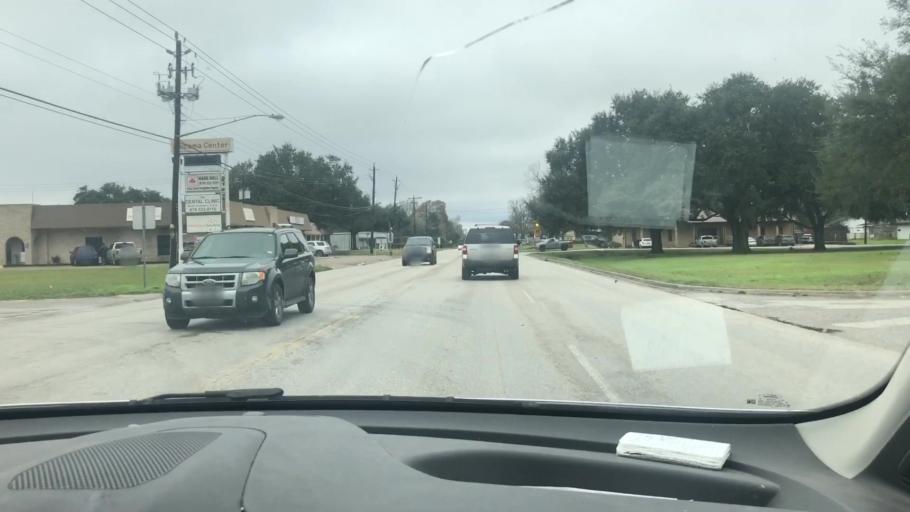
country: US
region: Texas
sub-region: Wharton County
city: Wharton
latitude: 29.3211
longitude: -96.0851
